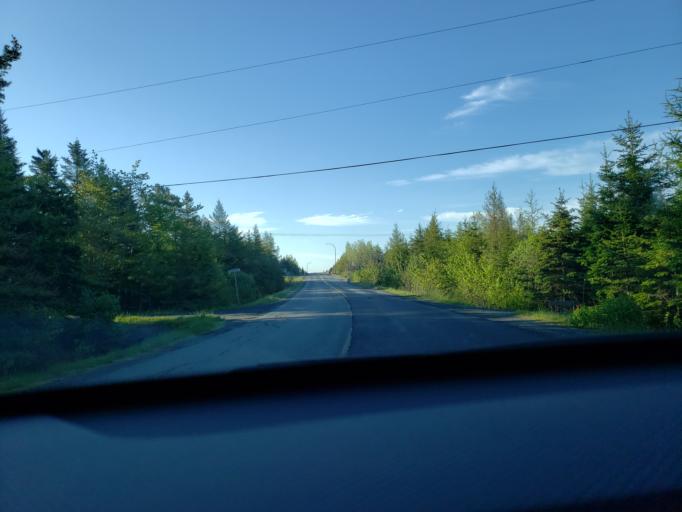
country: CA
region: Nova Scotia
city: Cole Harbour
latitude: 44.7150
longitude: -63.3967
